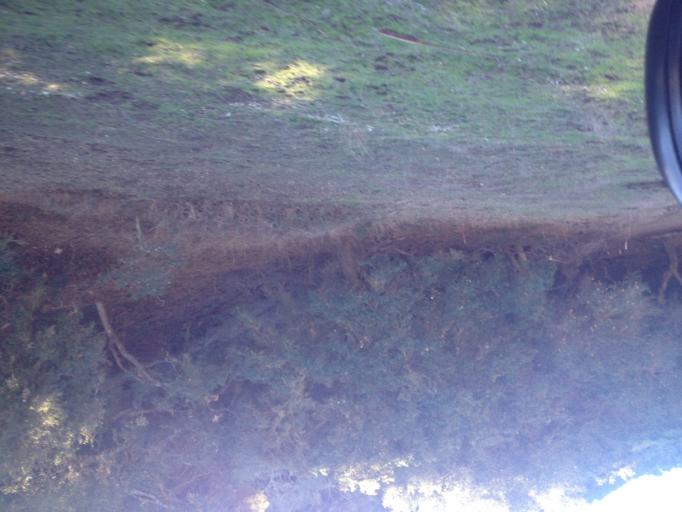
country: US
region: California
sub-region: San Luis Obispo County
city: Avila Beach
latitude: 35.2398
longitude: -120.7731
